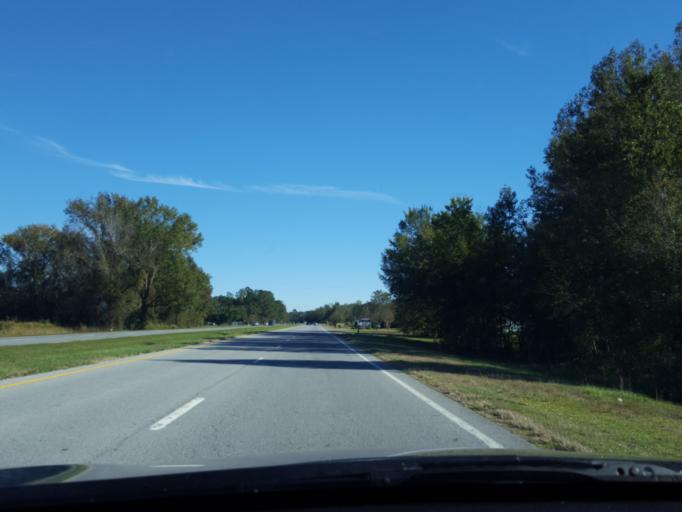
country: US
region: North Carolina
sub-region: Beaufort County
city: Washington
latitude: 35.6127
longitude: -77.1577
